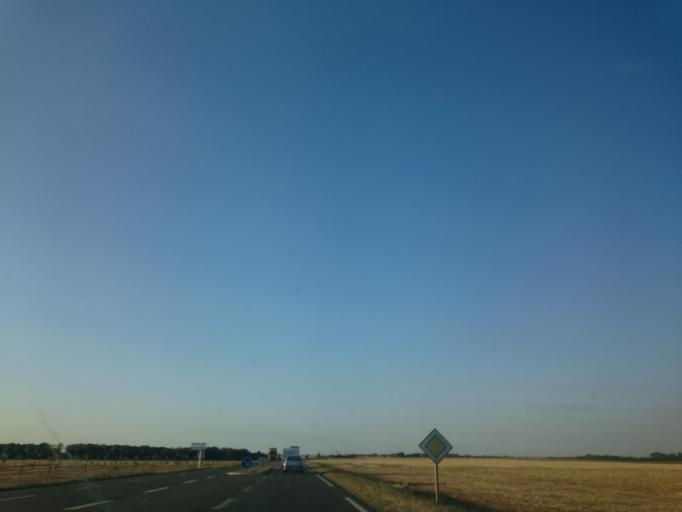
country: FR
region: Ile-de-France
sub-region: Departement de l'Essonne
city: Angerville
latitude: 48.2791
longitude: 1.9778
